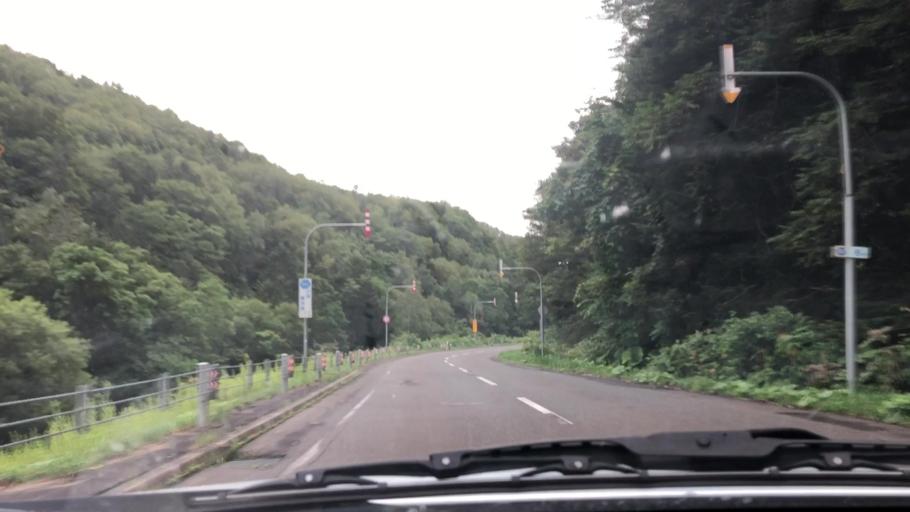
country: JP
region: Hokkaido
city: Shimo-furano
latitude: 42.9411
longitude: 142.3736
